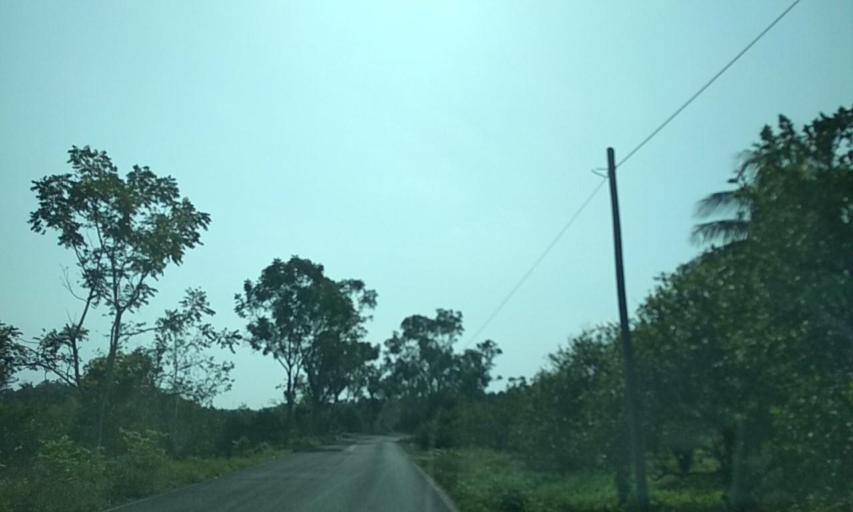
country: MX
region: Veracruz
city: Gutierrez Zamora
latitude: 20.3488
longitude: -97.1495
